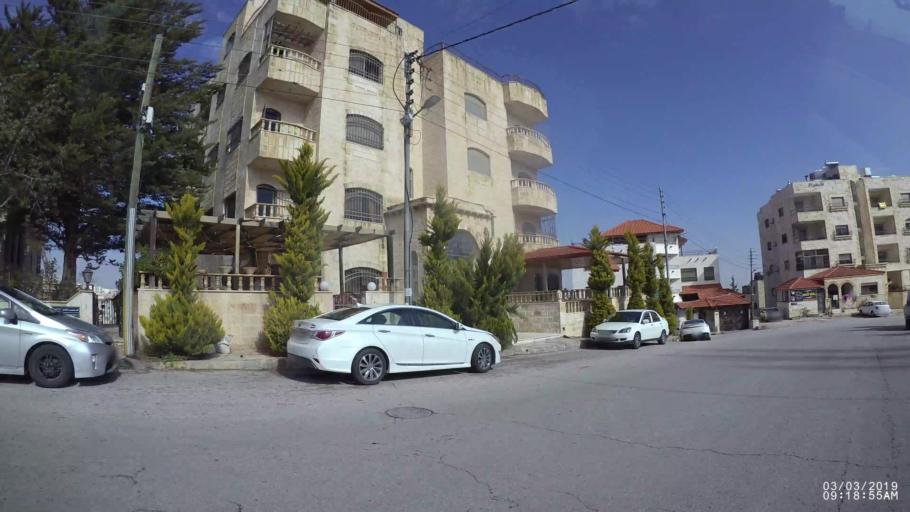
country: JO
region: Amman
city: Al Jubayhah
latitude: 32.0005
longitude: 35.8903
